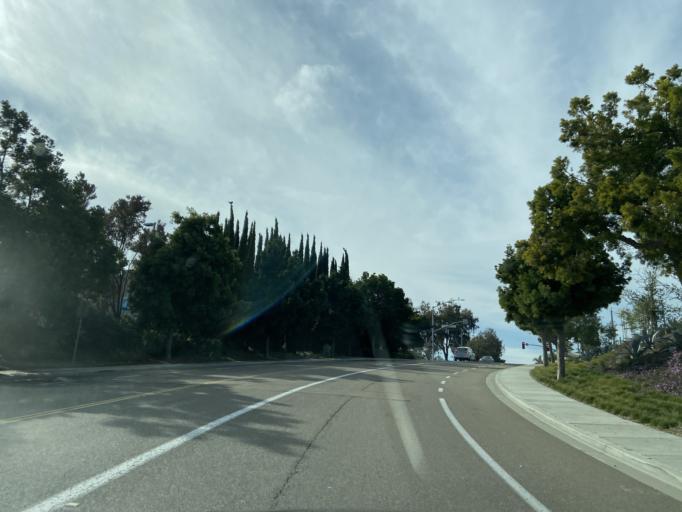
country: US
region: California
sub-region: San Diego County
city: Lake San Marcos
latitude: 33.1236
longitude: -117.2653
